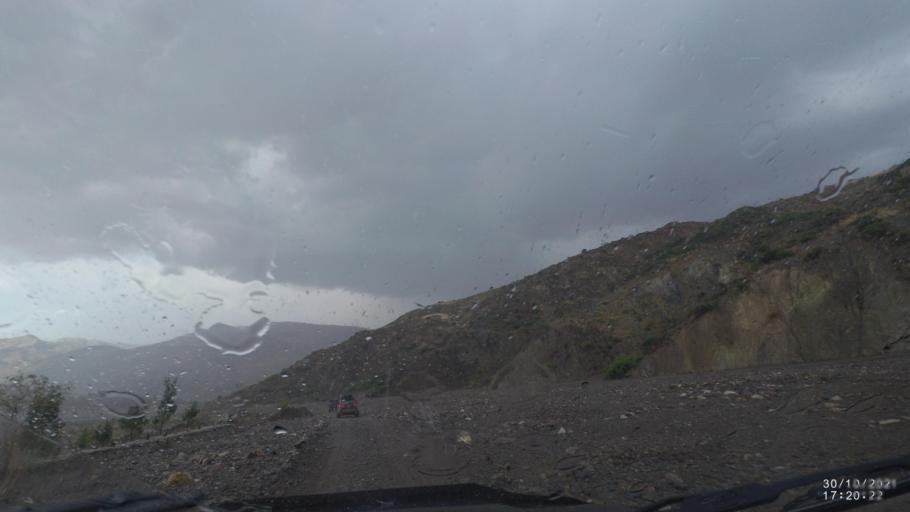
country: BO
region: Cochabamba
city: Colchani
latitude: -17.5312
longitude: -66.6193
